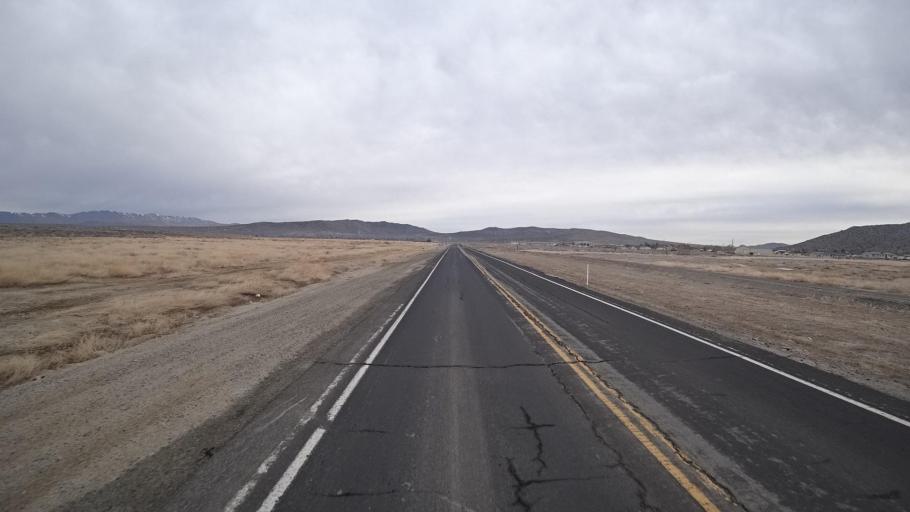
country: US
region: Nevada
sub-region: Washoe County
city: Lemmon Valley
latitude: 39.6561
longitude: -119.8284
